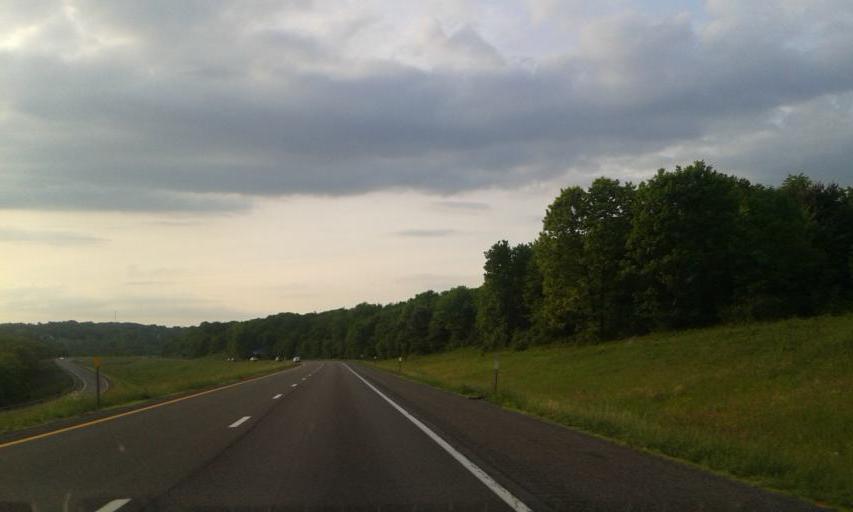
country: US
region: New York
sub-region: Broome County
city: Chenango Bridge
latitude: 42.2208
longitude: -75.9069
